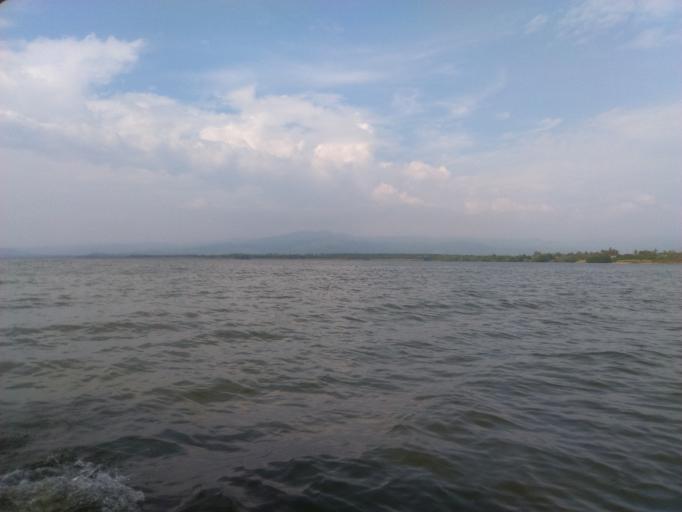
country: MX
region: Guerrero
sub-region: Coyuca de Benitez
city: Colonia Luces en el Mar
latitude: 16.9092
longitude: -99.9747
